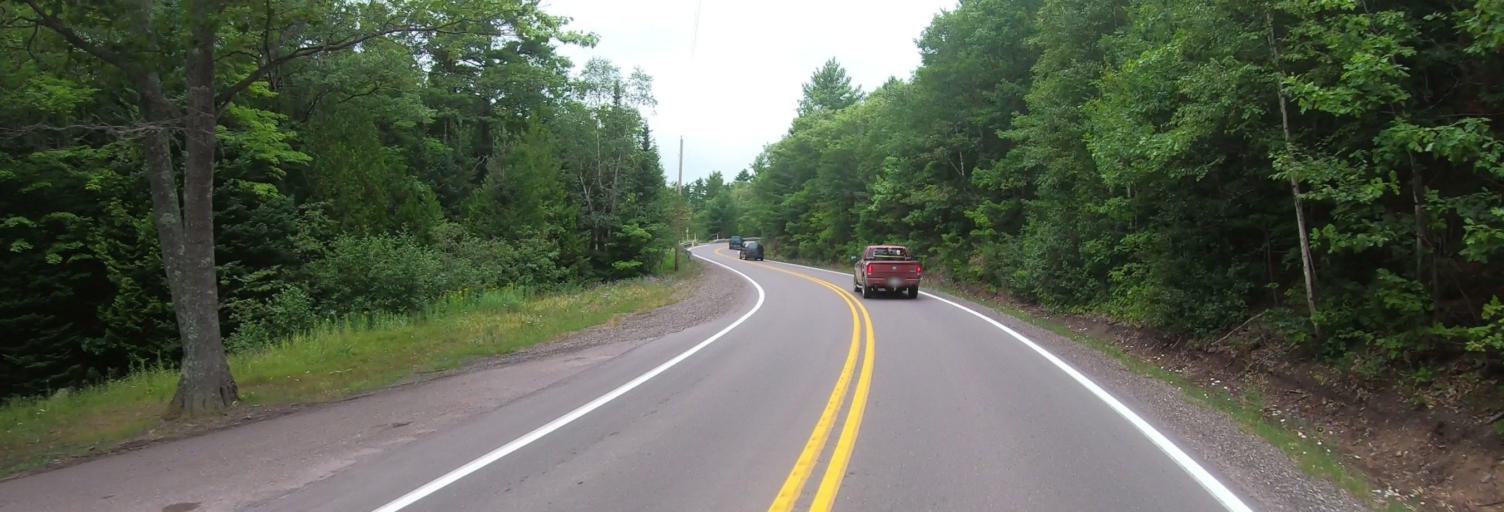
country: US
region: Michigan
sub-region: Keweenaw County
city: Eagle River
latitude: 47.4305
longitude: -87.9827
